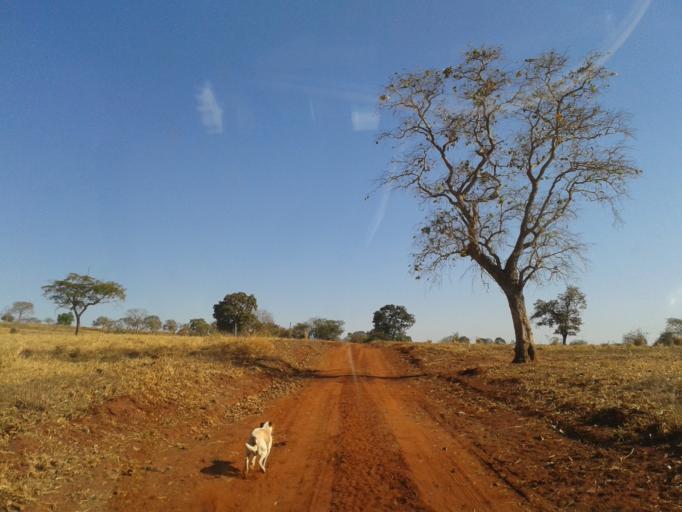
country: BR
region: Minas Gerais
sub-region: Santa Vitoria
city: Santa Vitoria
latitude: -19.0590
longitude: -49.9268
